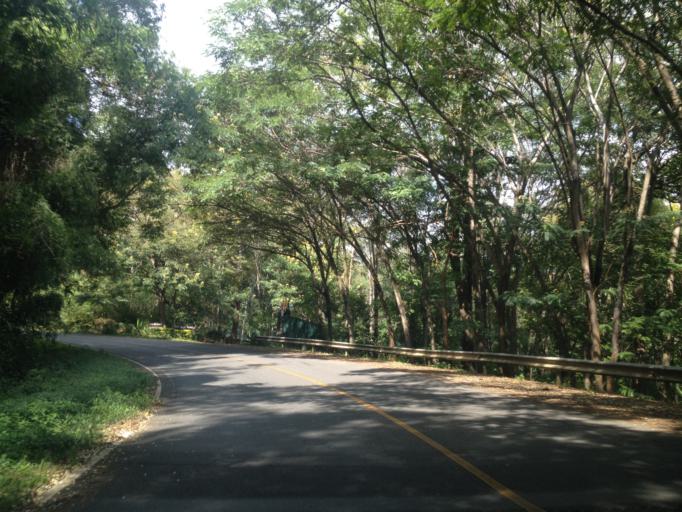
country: TH
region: Chiang Mai
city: Samoeng
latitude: 18.8366
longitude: 98.7831
